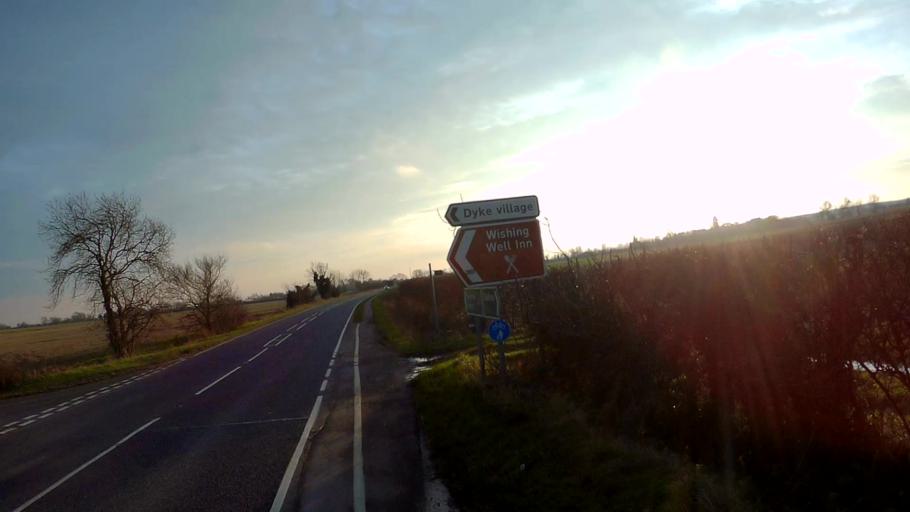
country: GB
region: England
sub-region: Lincolnshire
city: Bourne
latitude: 52.7890
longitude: -0.3765
